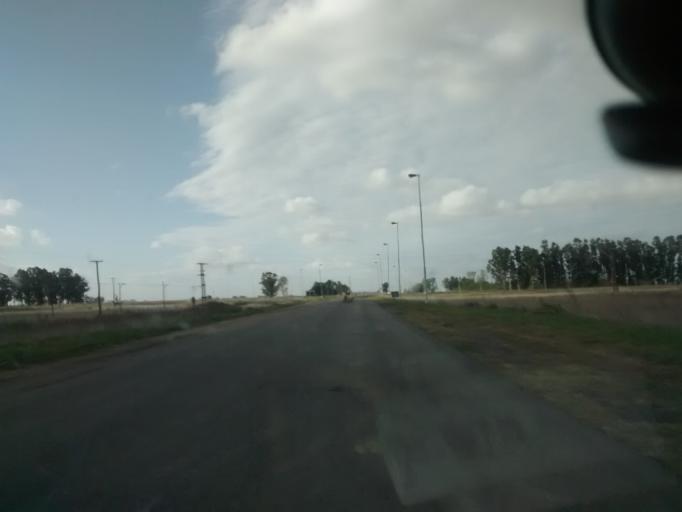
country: AR
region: Buenos Aires
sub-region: Partido de Ayacucho
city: Ayacucho
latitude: -37.1306
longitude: -58.5519
